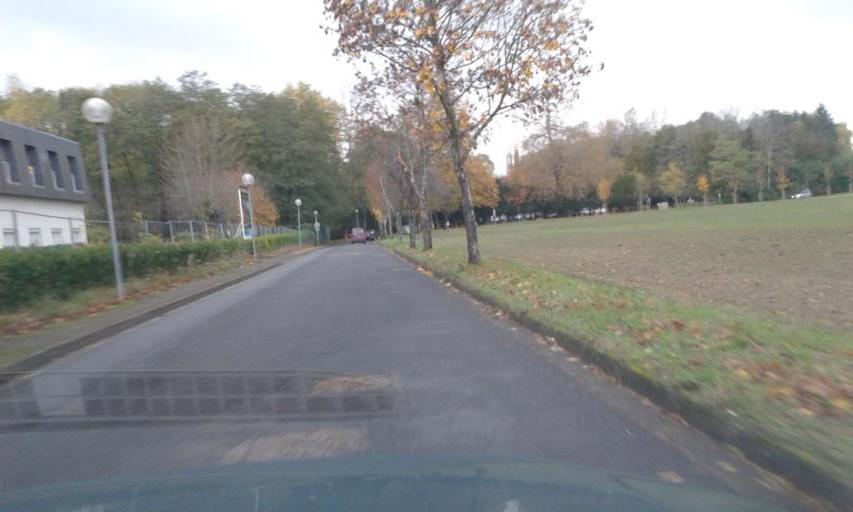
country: FR
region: Centre
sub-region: Departement du Loiret
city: Olivet
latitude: 47.8701
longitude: 1.8887
